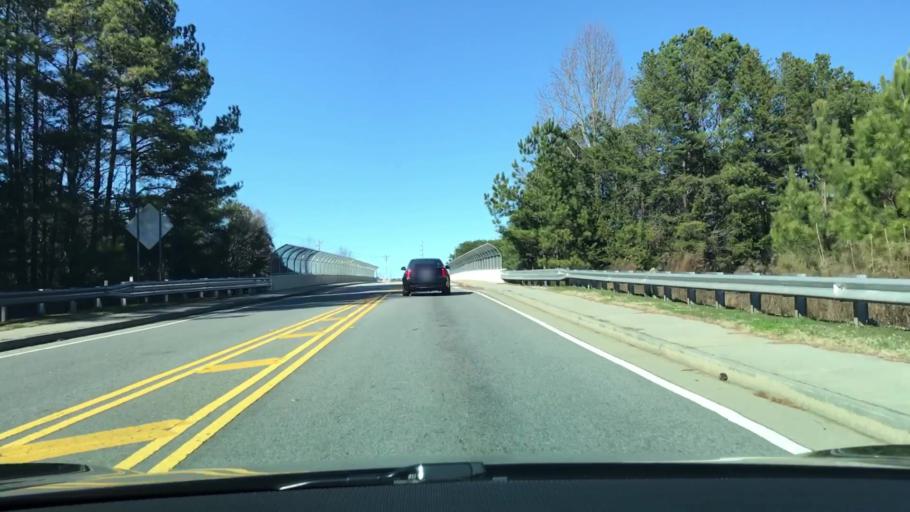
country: US
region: Georgia
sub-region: Forsyth County
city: Cumming
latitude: 34.1929
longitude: -84.1314
